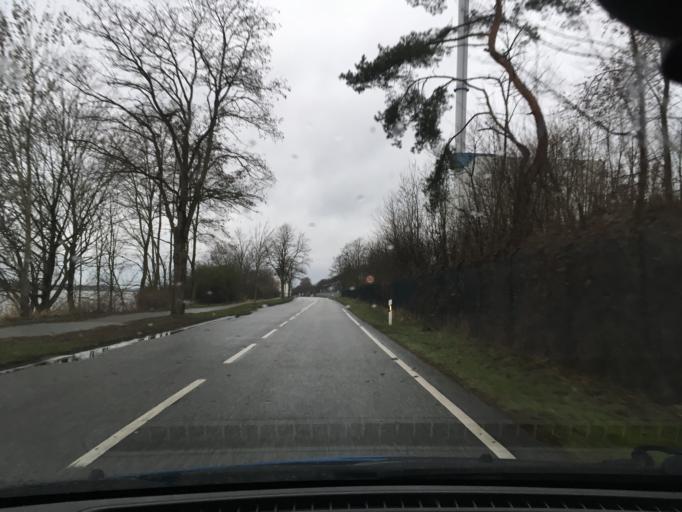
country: DE
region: Lower Saxony
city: Tespe
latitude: 53.4083
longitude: 10.4115
